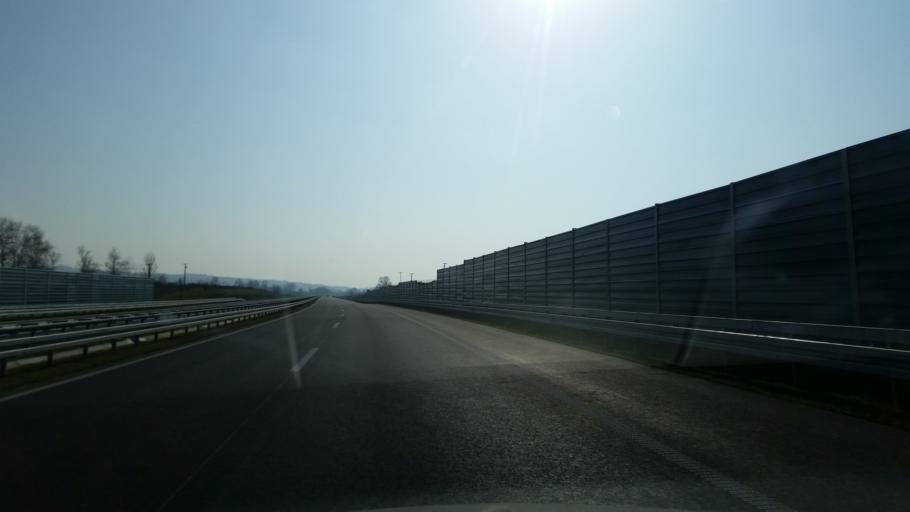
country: RS
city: Prislonica
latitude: 43.9613
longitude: 20.3967
